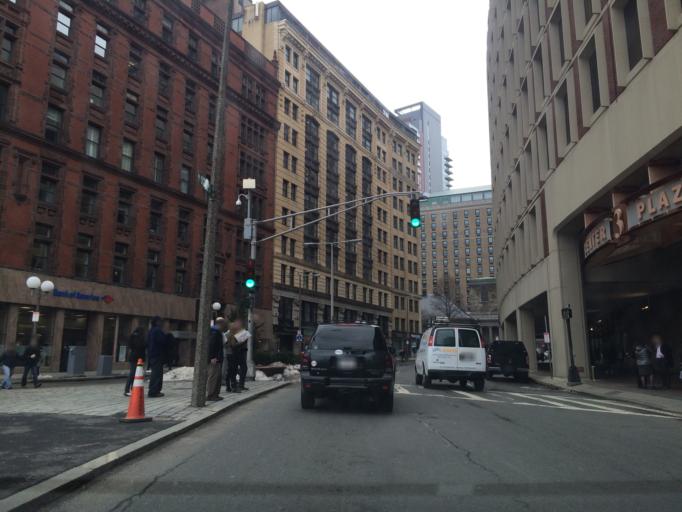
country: US
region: Massachusetts
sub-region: Suffolk County
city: Boston
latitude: 42.3595
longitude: -71.0599
